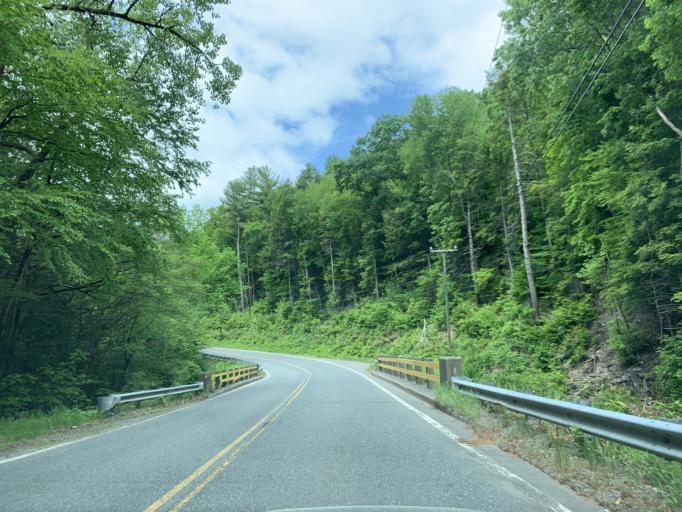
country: US
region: Massachusetts
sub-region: Hampshire County
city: Westhampton
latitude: 42.2371
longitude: -72.8506
